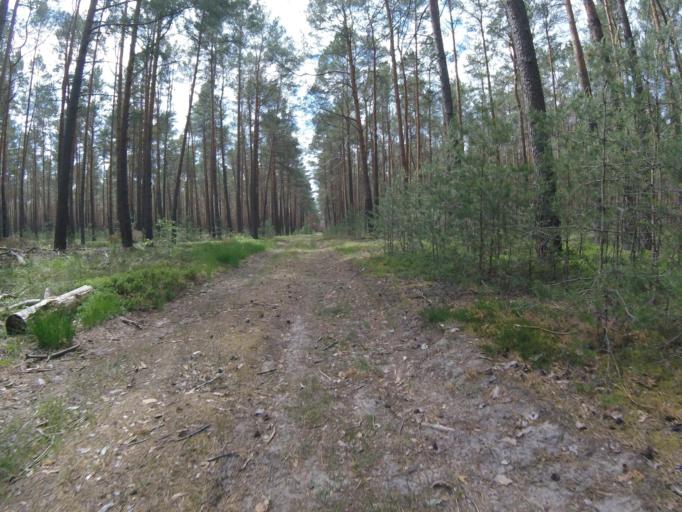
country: DE
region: Brandenburg
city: Halbe
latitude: 52.1027
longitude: 13.6603
